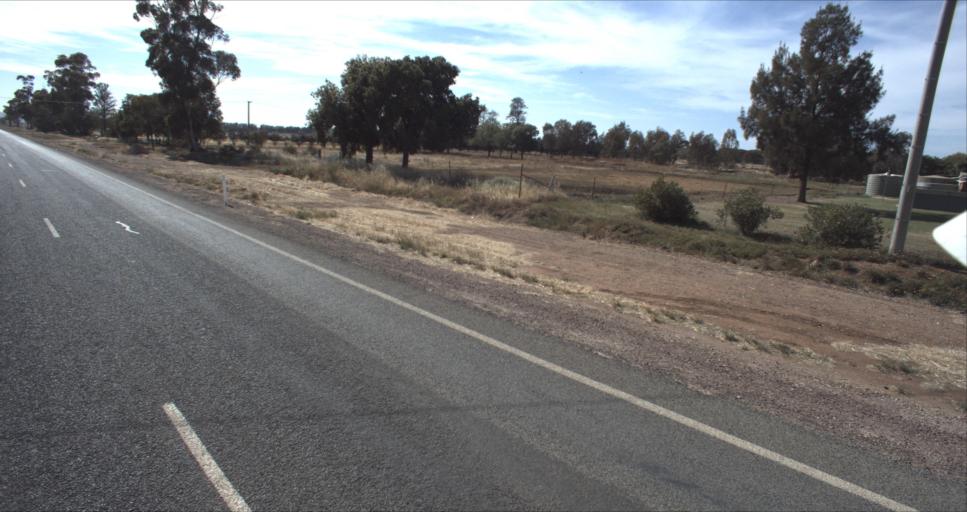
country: AU
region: New South Wales
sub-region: Leeton
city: Leeton
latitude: -34.5610
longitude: 146.4362
